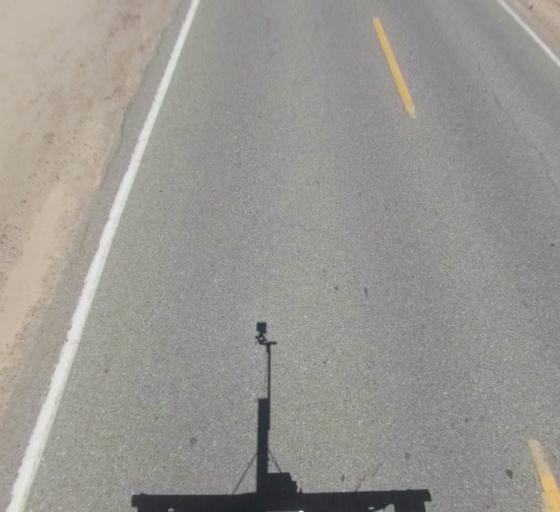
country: US
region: California
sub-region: Madera County
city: Bonadelle Ranchos-Madera Ranchos
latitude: 36.8754
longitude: -119.9113
